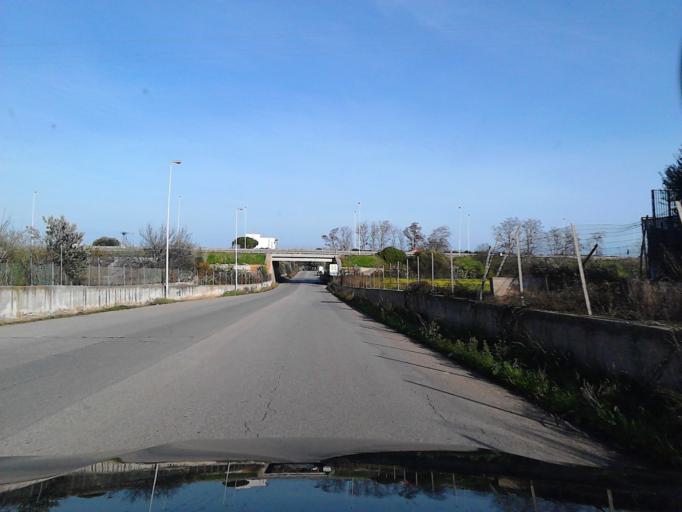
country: IT
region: Apulia
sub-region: Provincia di Bari
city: Mola di Bari
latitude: 41.0499
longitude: 17.0725
